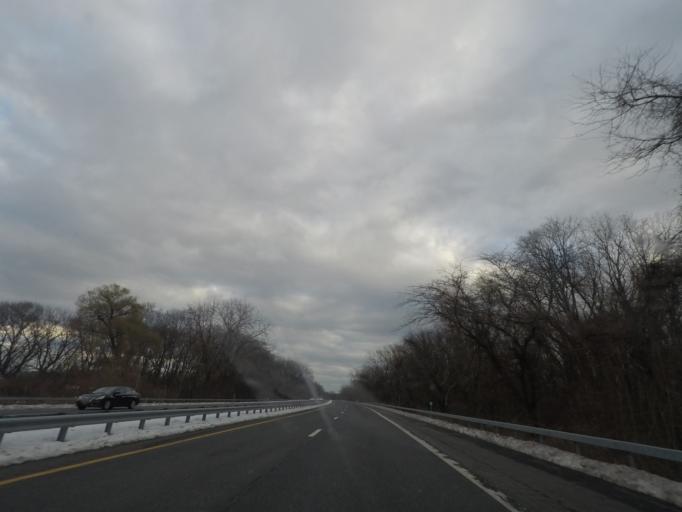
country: US
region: New York
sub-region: Ulster County
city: Kingston
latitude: 41.9408
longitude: -74.0229
